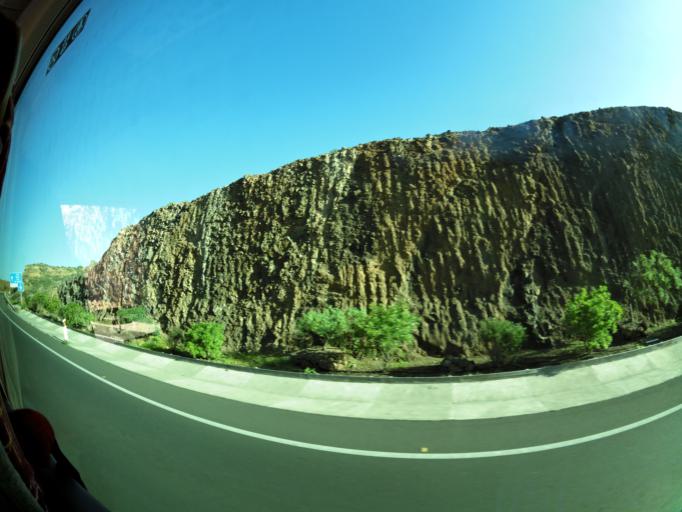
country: ES
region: Canary Islands
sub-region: Provincia de Las Palmas
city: Agaete
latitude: 28.1174
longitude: -15.6784
